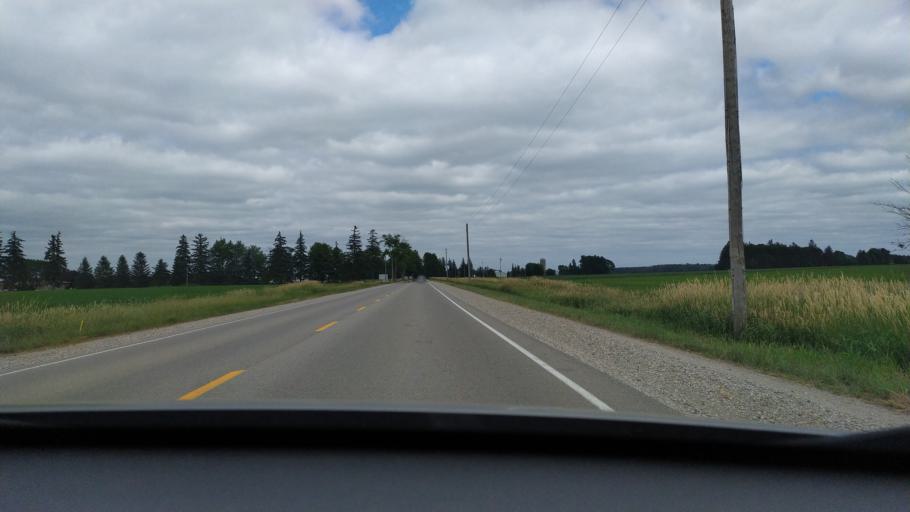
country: CA
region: Ontario
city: Stratford
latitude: 43.3161
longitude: -80.9736
